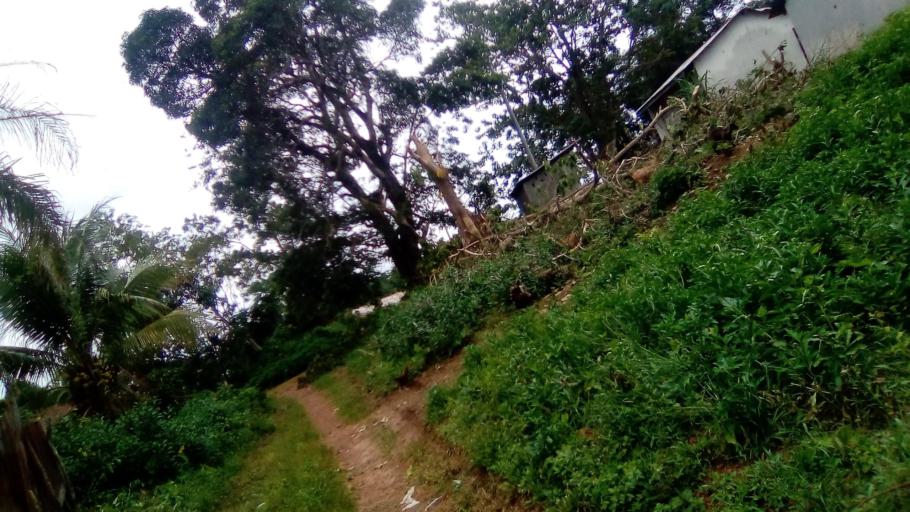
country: SL
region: Southern Province
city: Pujehun
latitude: 7.3631
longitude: -11.7081
